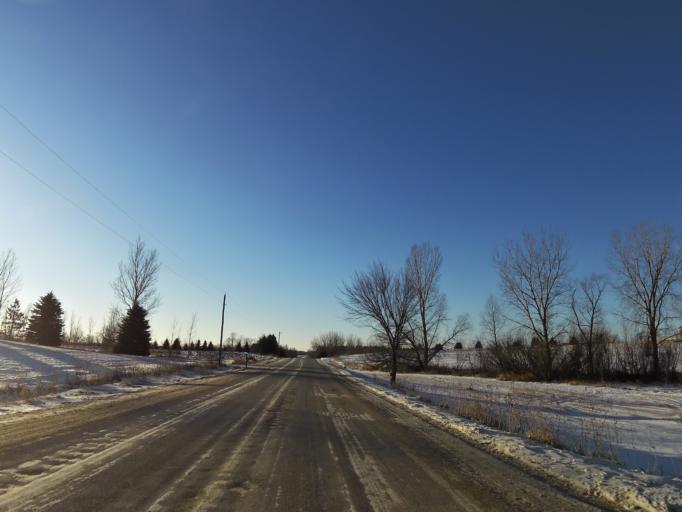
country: US
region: Minnesota
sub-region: Scott County
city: Jordan
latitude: 44.6414
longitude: -93.5164
